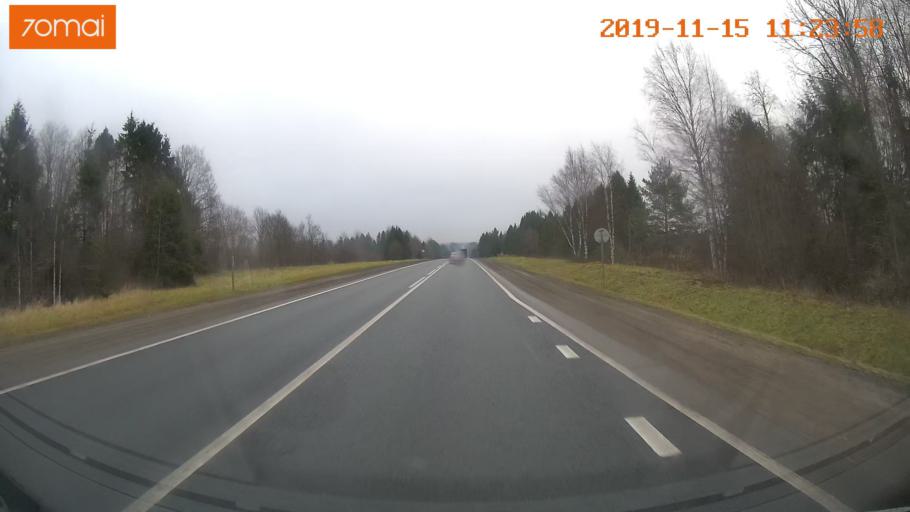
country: RU
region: Vologda
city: Molochnoye
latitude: 59.1546
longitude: 39.3947
